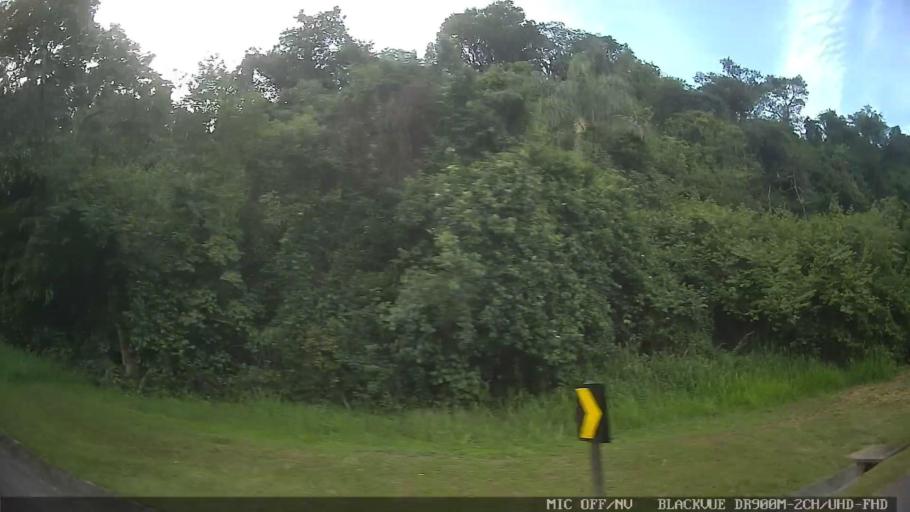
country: BR
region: Sao Paulo
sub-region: Porto Feliz
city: Porto Feliz
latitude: -23.2192
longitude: -47.5718
